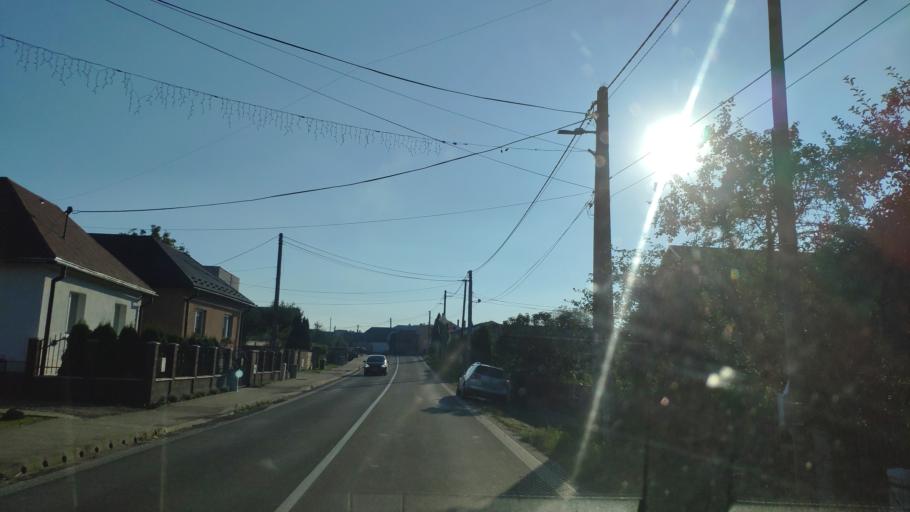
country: SK
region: Presovsky
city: Snina
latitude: 48.9798
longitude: 22.1089
